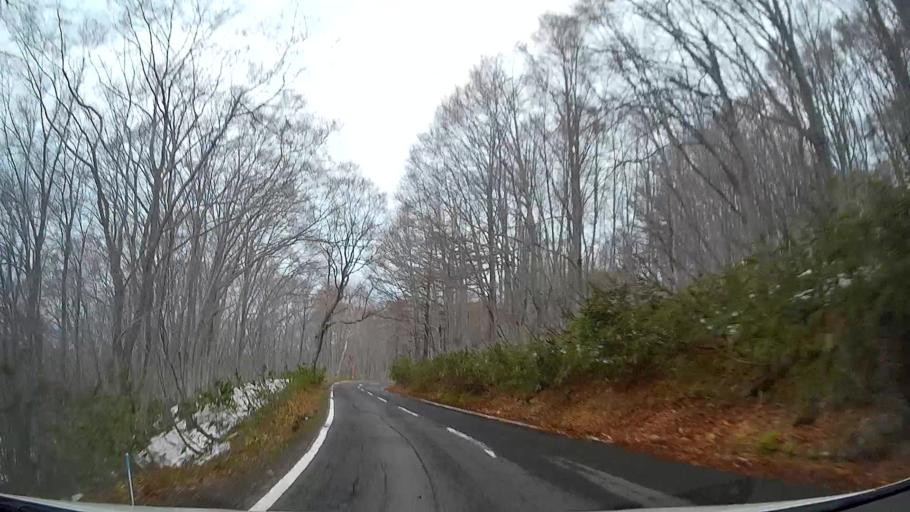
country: JP
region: Aomori
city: Aomori Shi
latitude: 40.6501
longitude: 140.8458
